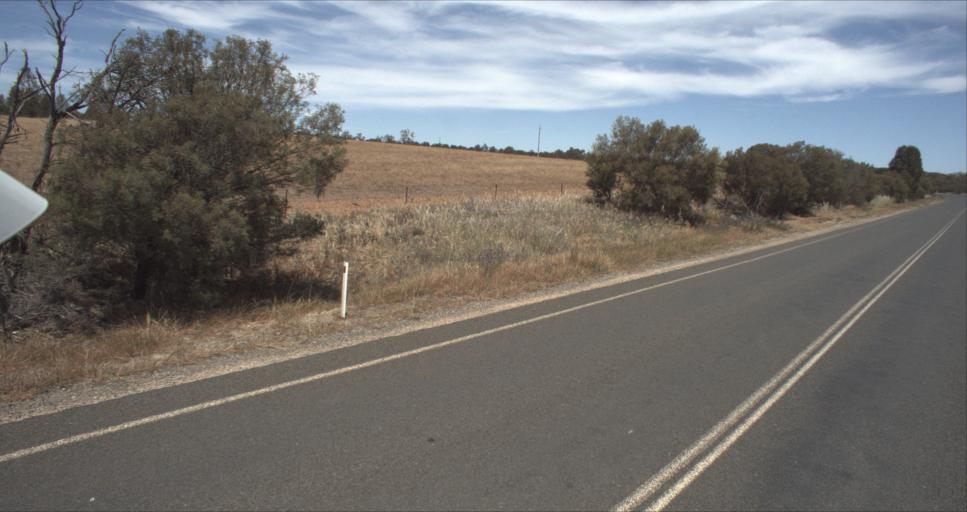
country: AU
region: New South Wales
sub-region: Leeton
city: Leeton
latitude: -34.6612
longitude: 146.4516
